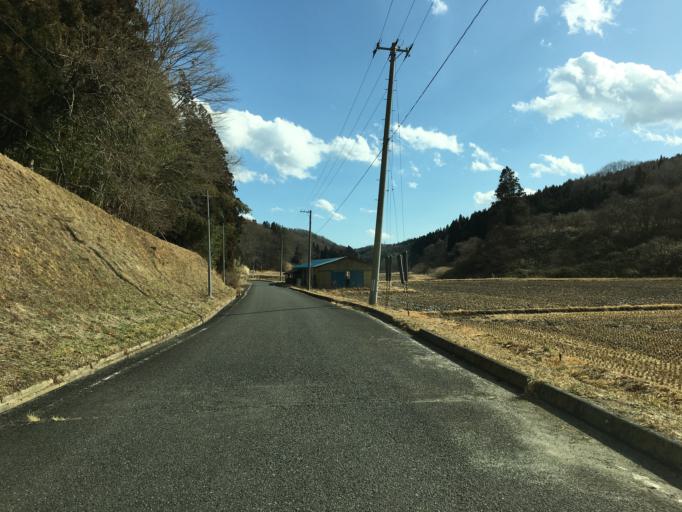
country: JP
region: Fukushima
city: Ishikawa
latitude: 37.2350
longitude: 140.5909
